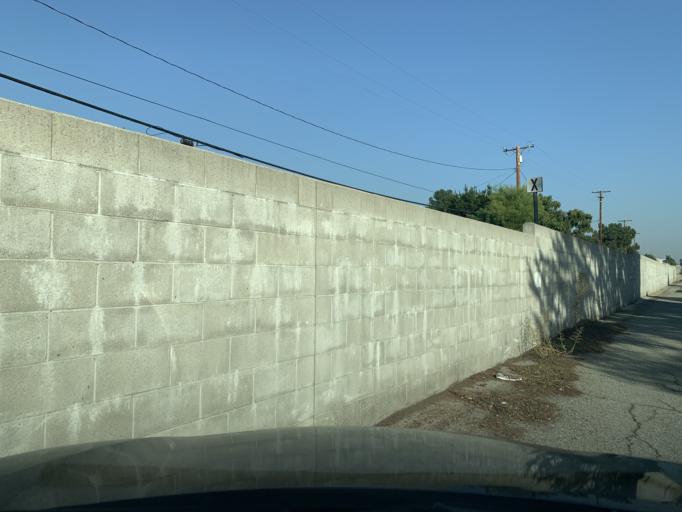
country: US
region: California
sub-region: Los Angeles County
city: Covina
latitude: 34.0920
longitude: -117.8946
